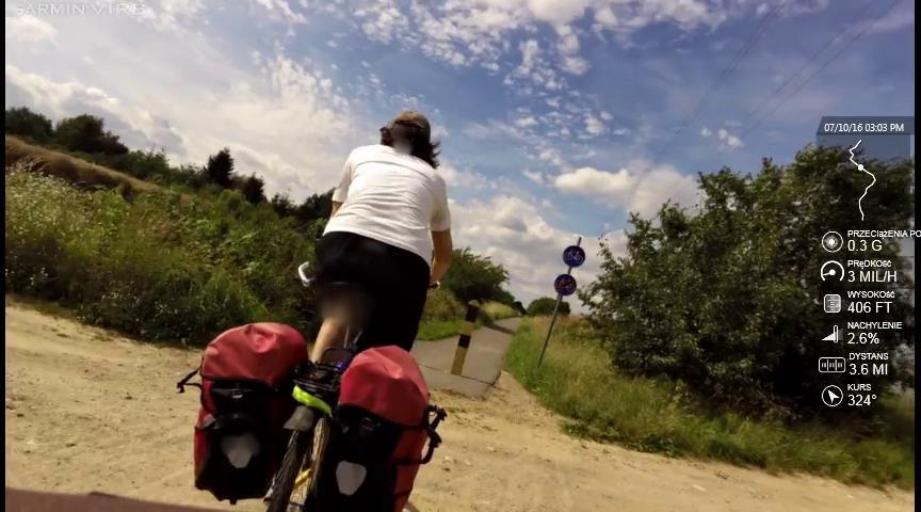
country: PL
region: West Pomeranian Voivodeship
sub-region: Powiat gryfinski
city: Banie
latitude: 53.1147
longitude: 14.6289
